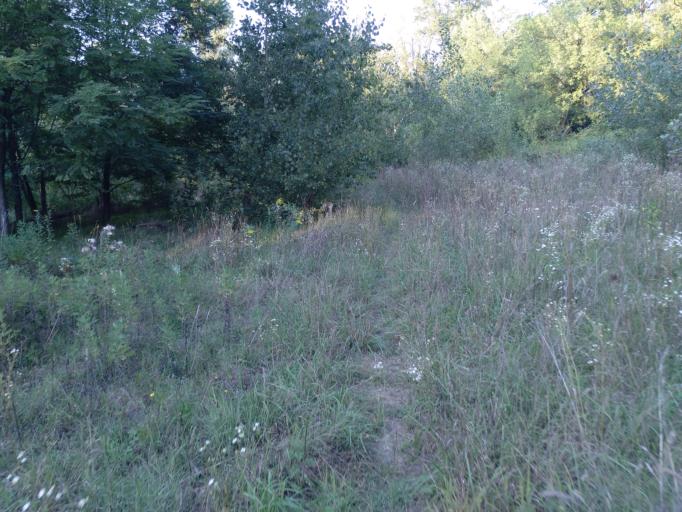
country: FR
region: Rhone-Alpes
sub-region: Departement du Rhone
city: Grigny
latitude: 45.6009
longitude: 4.7946
